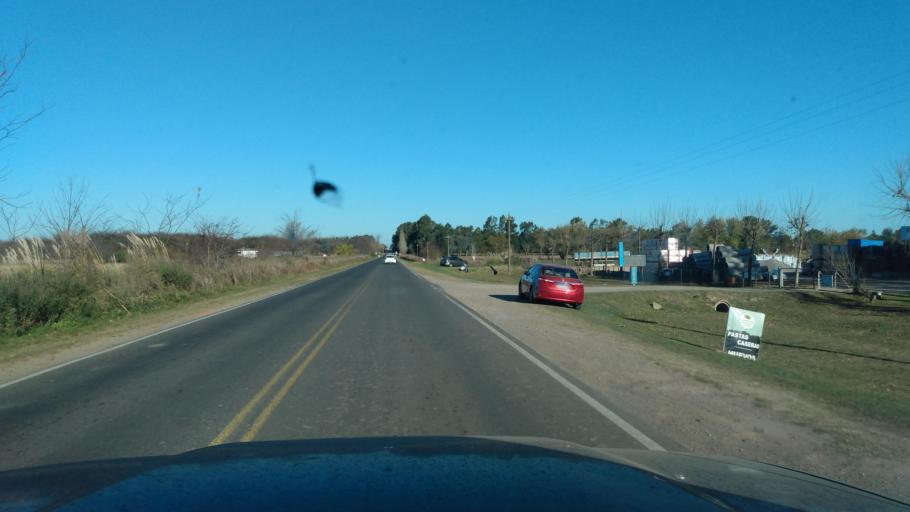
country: AR
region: Buenos Aires
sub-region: Partido de Lujan
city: Lujan
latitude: -34.5241
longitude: -59.1729
